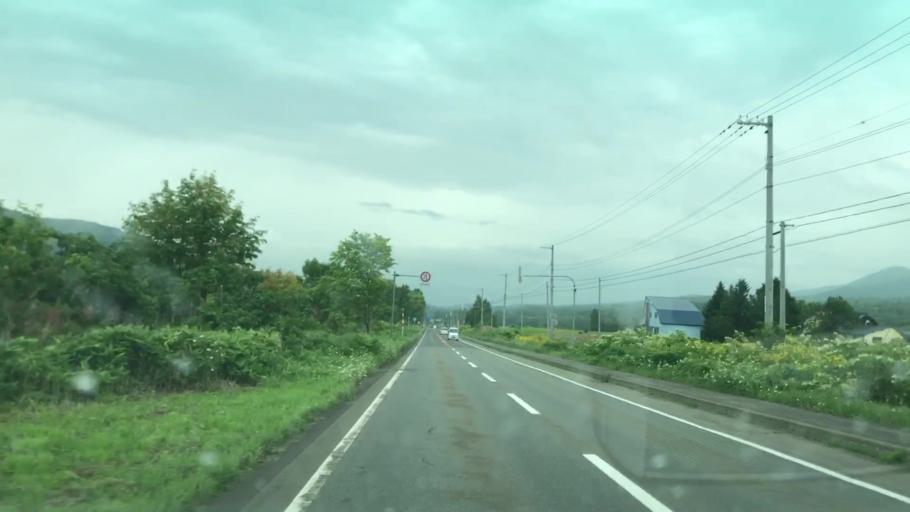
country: JP
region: Hokkaido
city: Niseko Town
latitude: 42.7651
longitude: 140.4824
